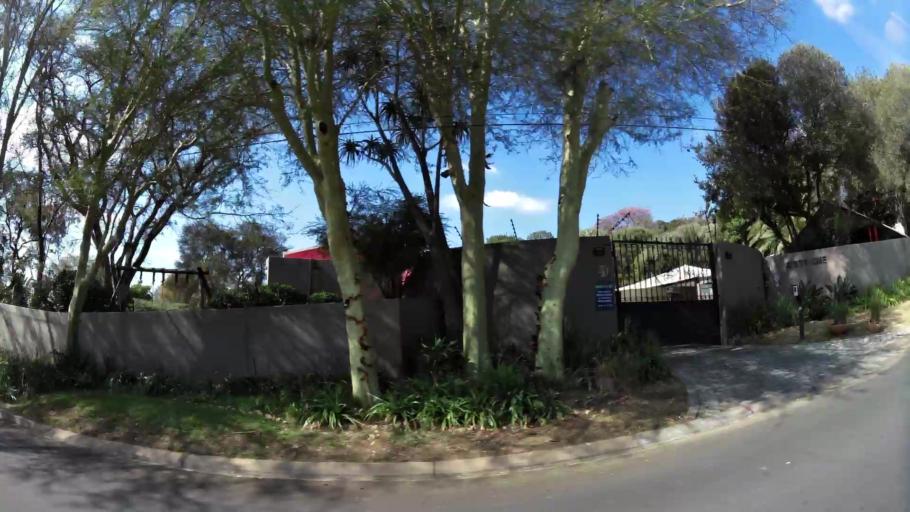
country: ZA
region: Gauteng
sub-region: City of Johannesburg Metropolitan Municipality
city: Roodepoort
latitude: -26.0848
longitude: 27.9540
